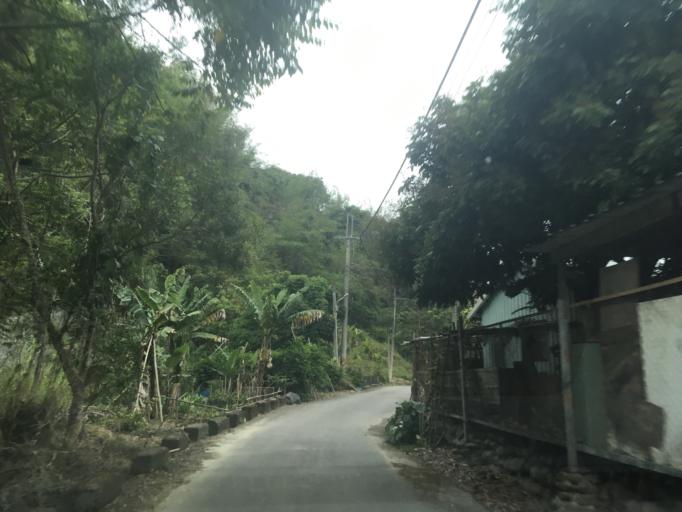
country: TW
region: Taiwan
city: Zhongxing New Village
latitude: 24.0382
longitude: 120.7565
